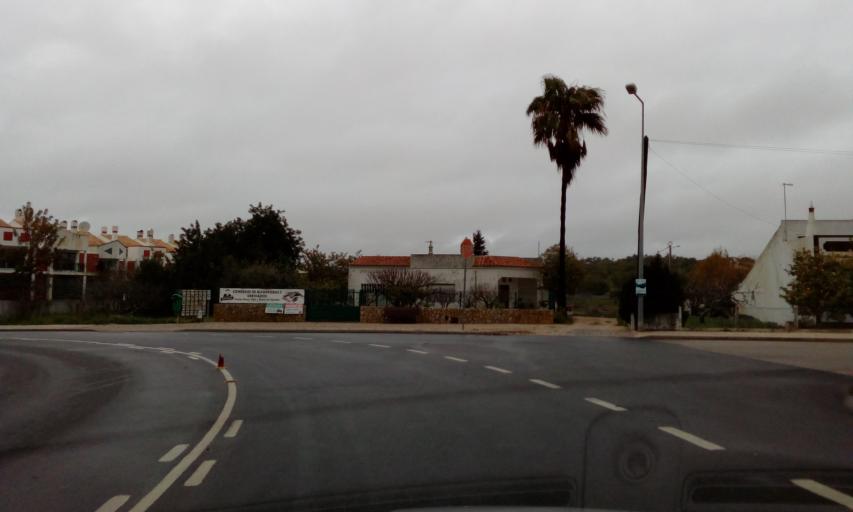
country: PT
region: Faro
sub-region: Albufeira
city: Ferreiras
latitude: 37.1241
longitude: -8.2238
